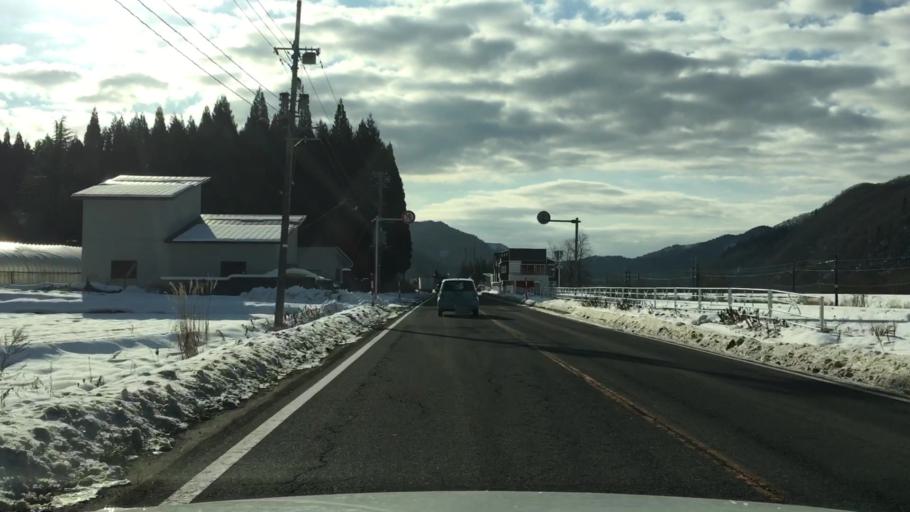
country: JP
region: Akita
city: Odate
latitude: 40.3589
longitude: 140.5976
